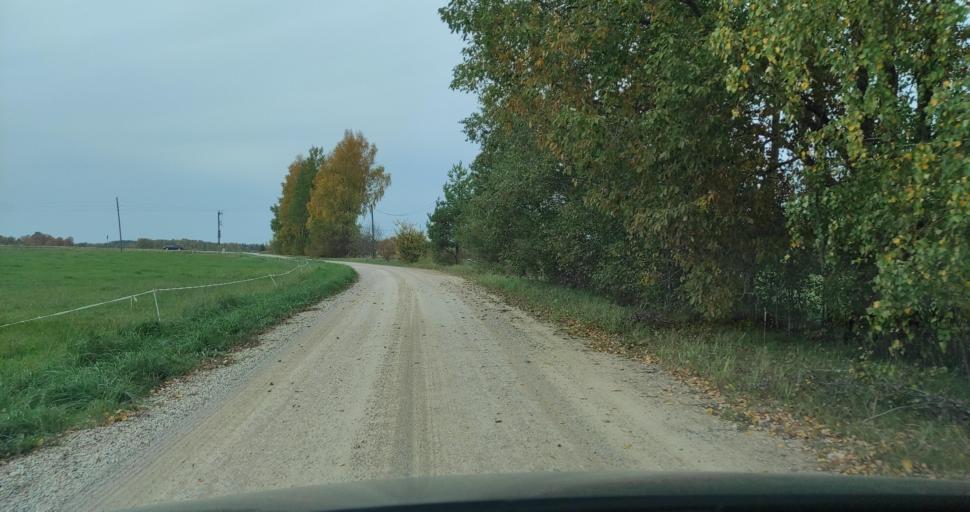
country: LV
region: Kuldigas Rajons
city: Kuldiga
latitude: 57.0280
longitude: 22.1974
